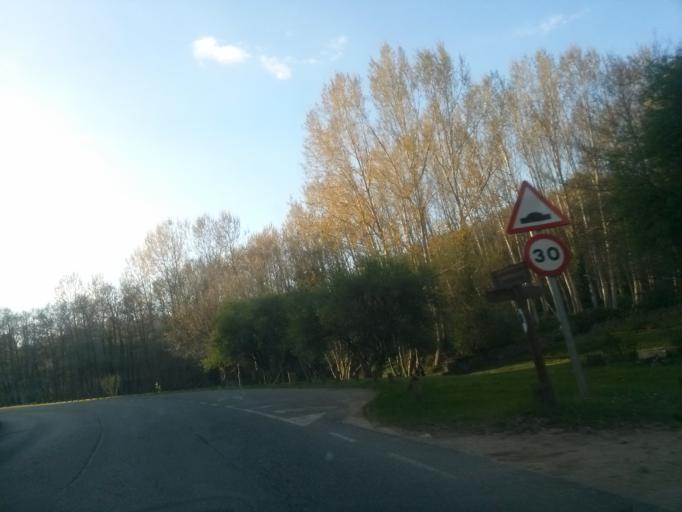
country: ES
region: Galicia
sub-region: Provincia de Lugo
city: Lugo
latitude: 43.0058
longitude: -7.5359
